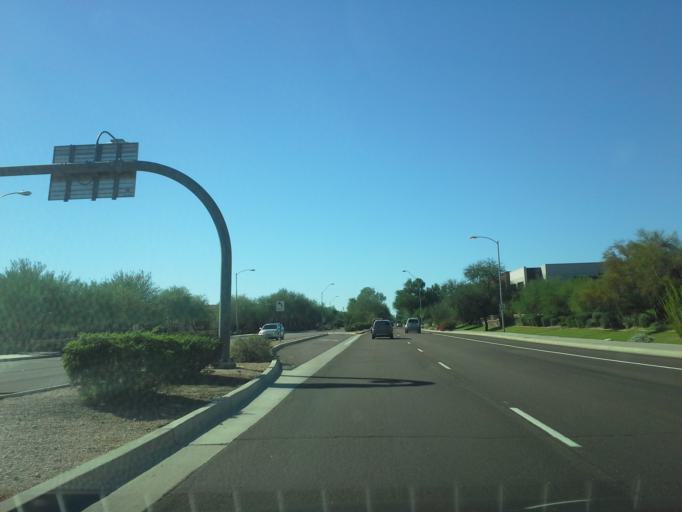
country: US
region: Arizona
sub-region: Maricopa County
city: Paradise Valley
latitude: 33.6401
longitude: -111.8919
